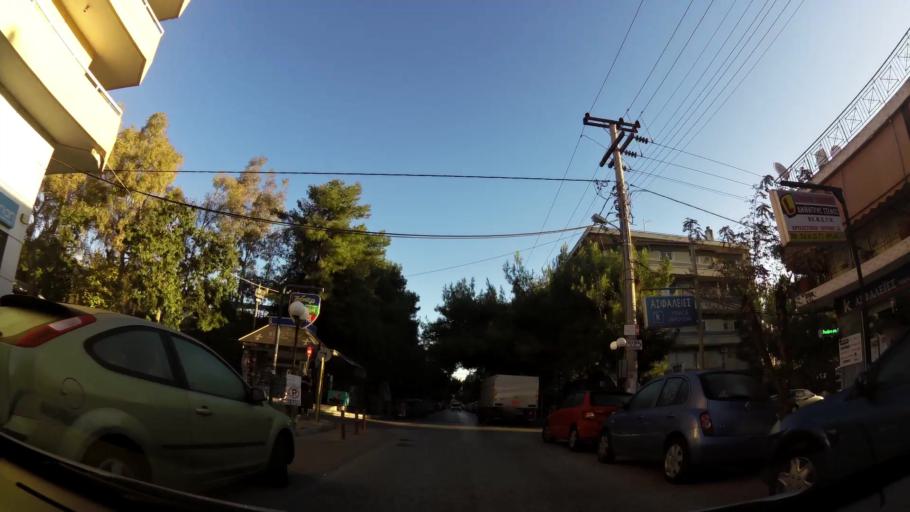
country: GR
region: Attica
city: Pefki
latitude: 38.0556
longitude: 23.7928
